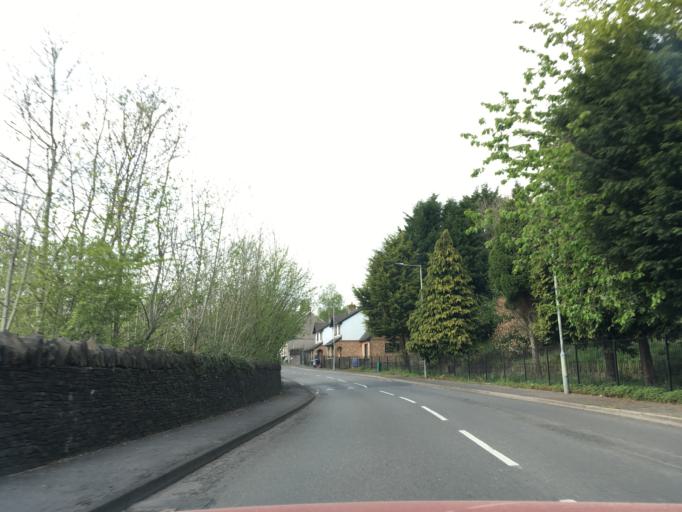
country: GB
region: Wales
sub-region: Merthyr Tydfil County Borough
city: Treharris
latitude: 51.6716
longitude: -3.2967
